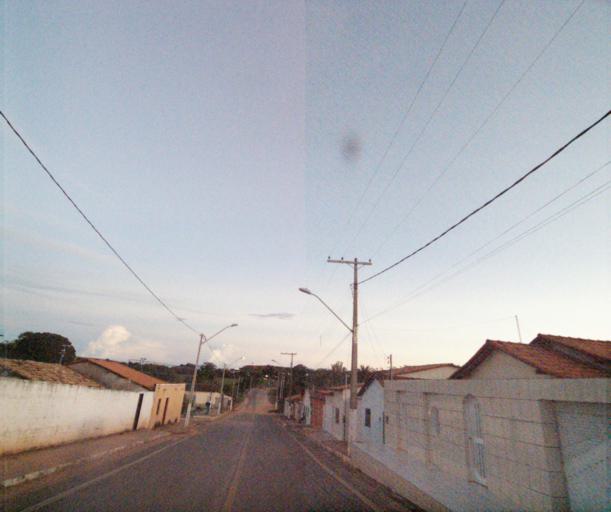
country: BR
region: Bahia
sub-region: Sao Felix Do Coribe
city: Santa Maria da Vitoria
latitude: -13.8316
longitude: -44.4539
